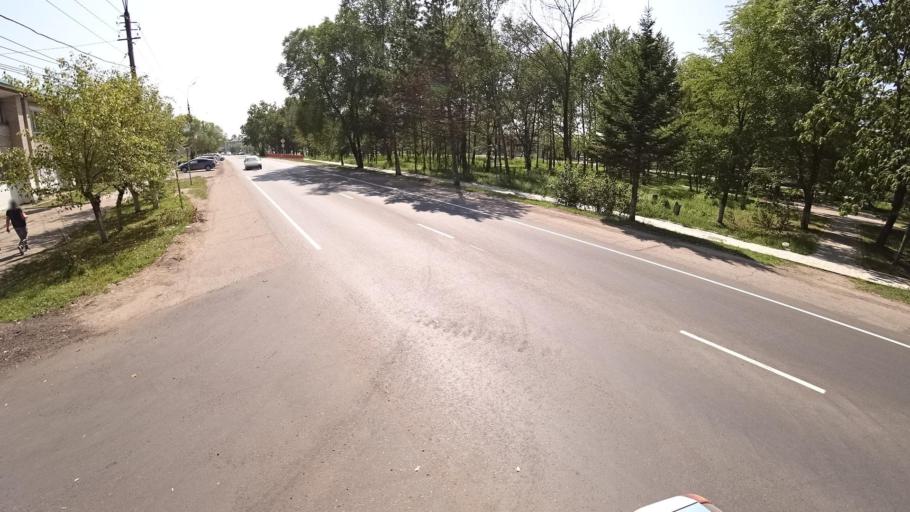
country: RU
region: Khabarovsk Krai
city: Khor
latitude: 47.9680
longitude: 135.0537
